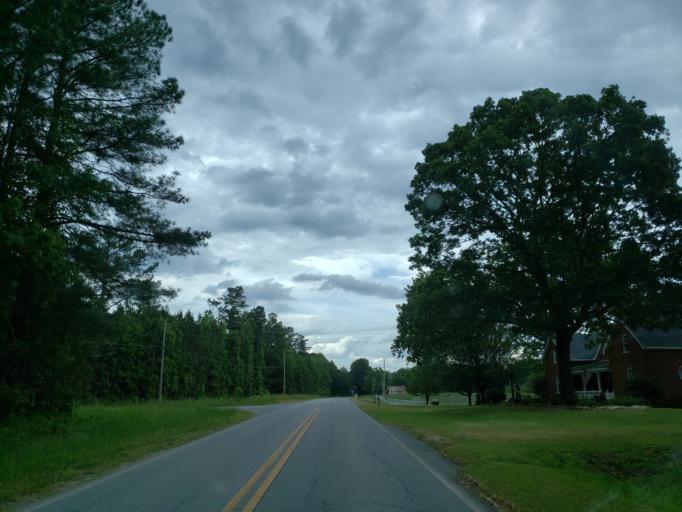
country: US
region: Georgia
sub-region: Polk County
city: Rockmart
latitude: 33.9336
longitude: -85.0521
